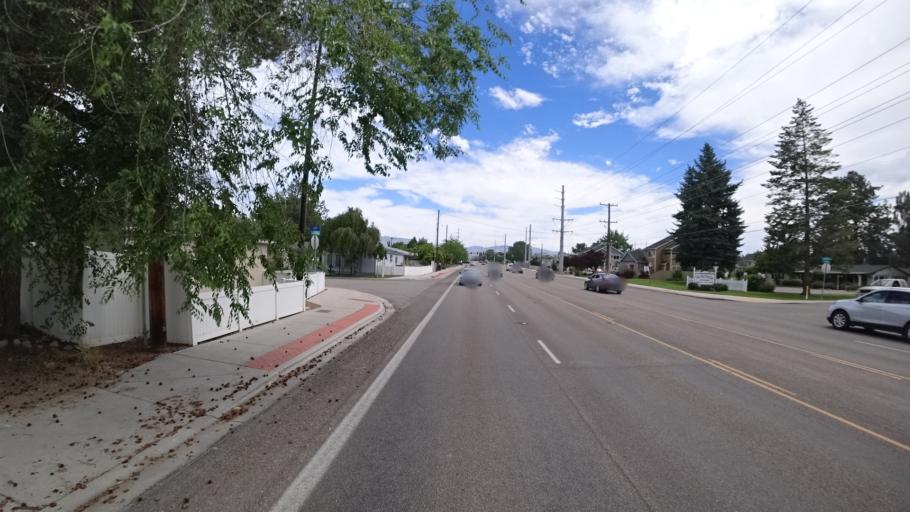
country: US
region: Idaho
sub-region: Ada County
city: Garden City
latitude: 43.6340
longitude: -116.2968
